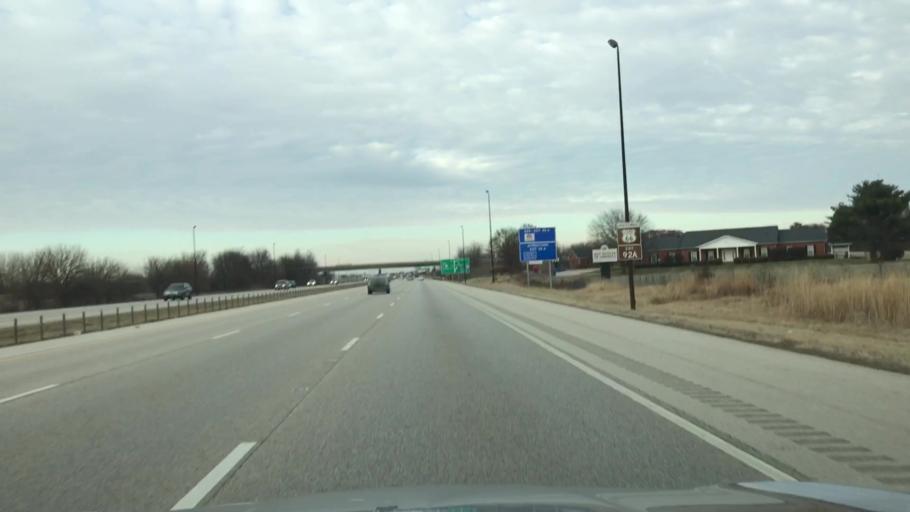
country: US
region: Illinois
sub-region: Sangamon County
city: Southern View
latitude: 39.7253
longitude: -89.6439
